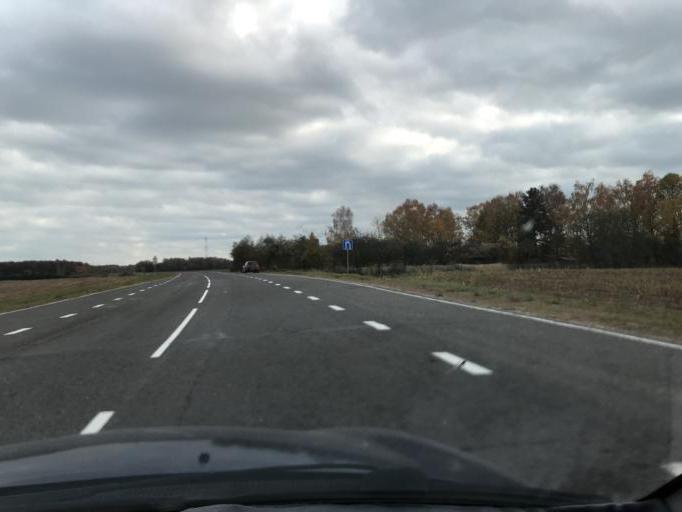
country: BY
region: Grodnenskaya
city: Lida
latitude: 53.7578
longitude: 25.1918
